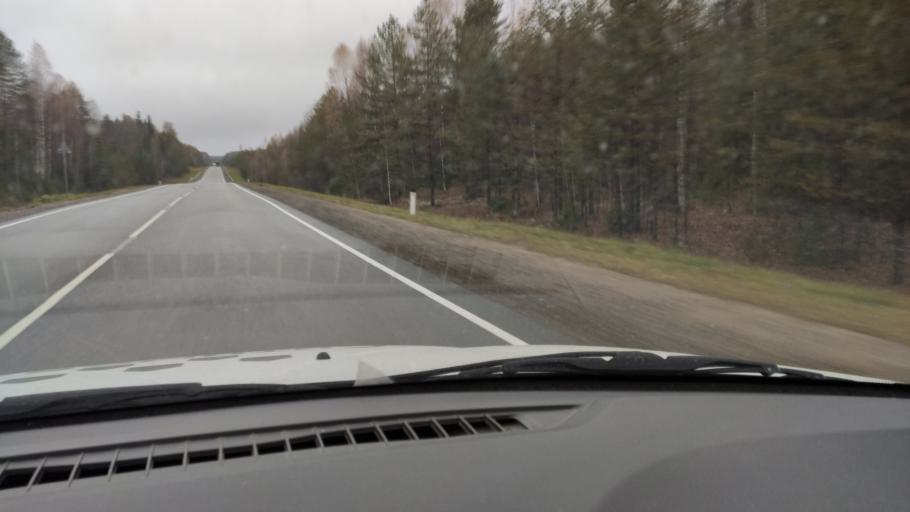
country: RU
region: Kirov
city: Chernaya Kholunitsa
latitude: 58.8223
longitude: 51.8034
